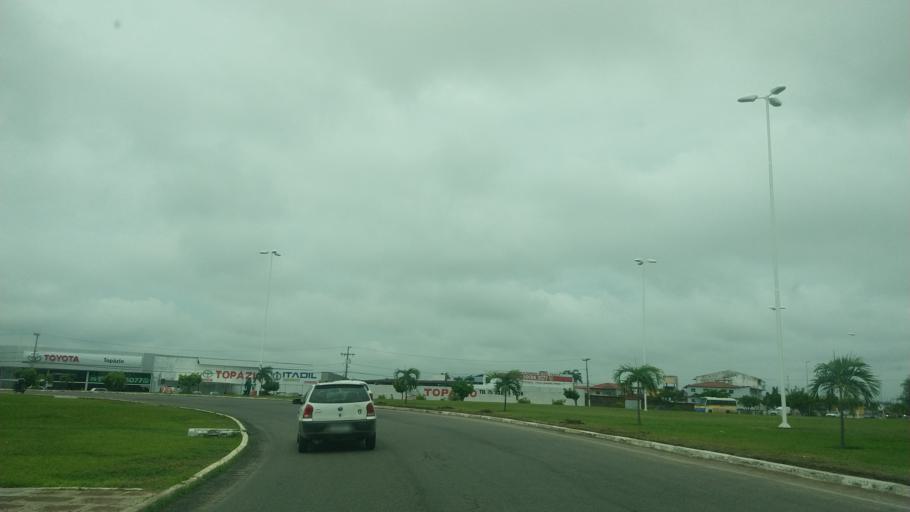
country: BR
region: Bahia
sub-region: Paulo Afonso
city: Paulo Afonso
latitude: -9.4009
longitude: -38.2385
